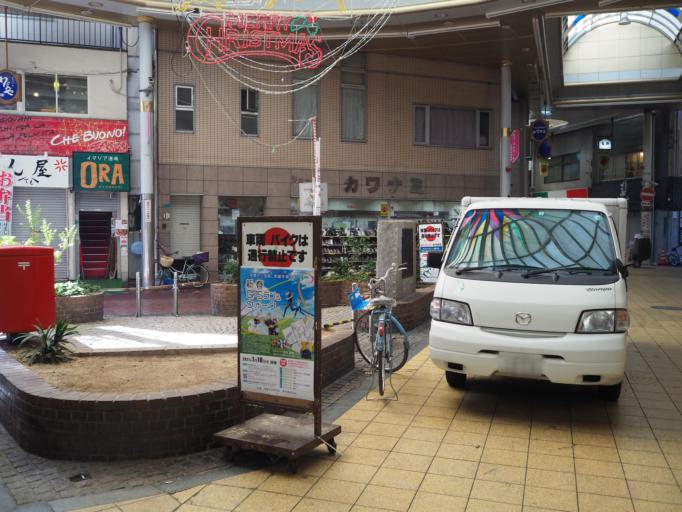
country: JP
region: Osaka
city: Osaka-shi
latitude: 34.7004
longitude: 135.5342
